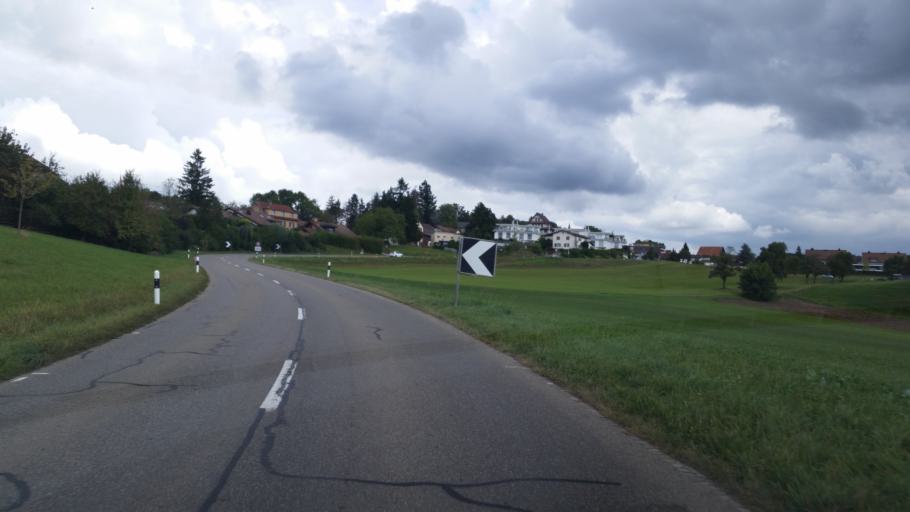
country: CH
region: Aargau
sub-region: Bezirk Bremgarten
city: Oberlunkhofen
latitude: 47.3150
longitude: 8.4131
